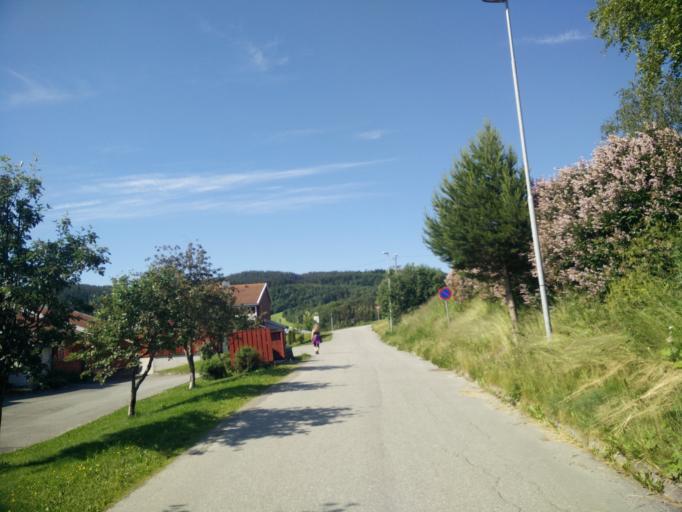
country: NO
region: Sor-Trondelag
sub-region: Skaun
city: Borsa
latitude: 63.3265
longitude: 10.0644
